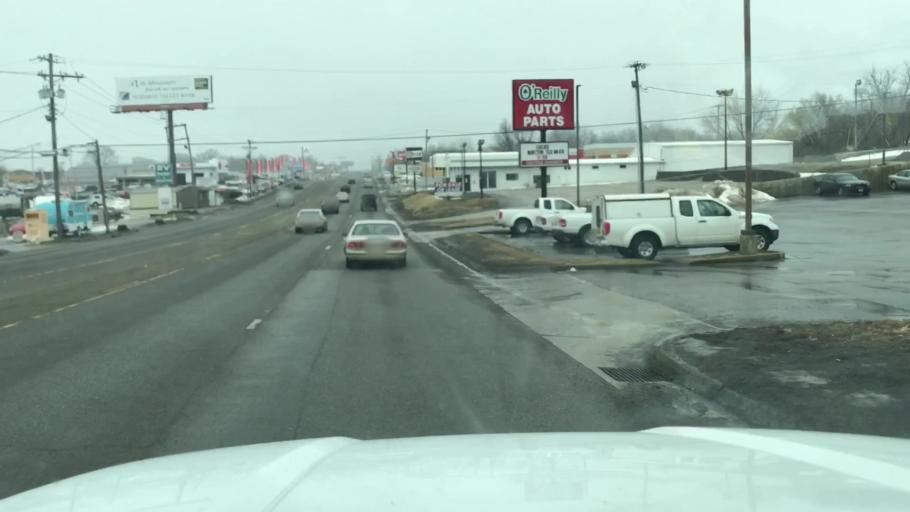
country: US
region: Missouri
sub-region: Buchanan County
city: Saint Joseph
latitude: 39.7574
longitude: -94.8037
